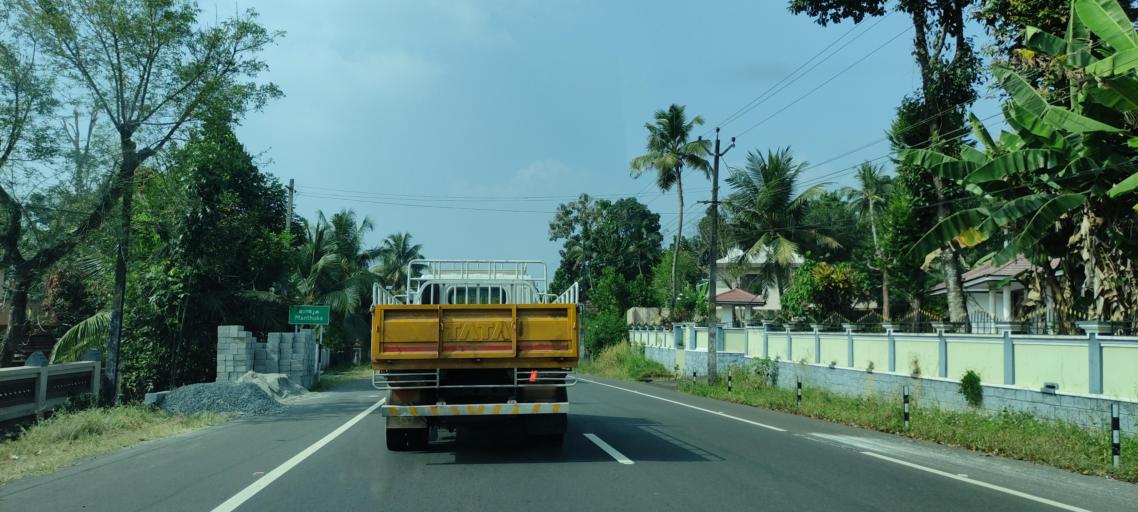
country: IN
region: Kerala
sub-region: Alappuzha
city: Chengannur
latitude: 9.2534
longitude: 76.6629
